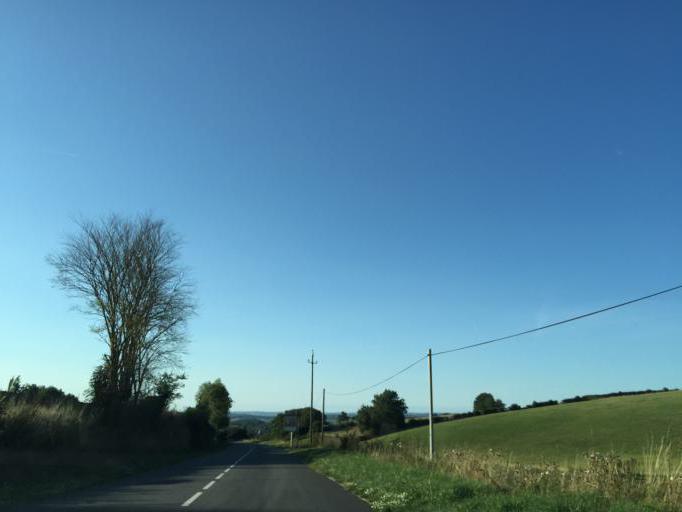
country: FR
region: Midi-Pyrenees
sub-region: Departement de l'Aveyron
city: Salles-Curan
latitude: 44.1658
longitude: 2.7957
